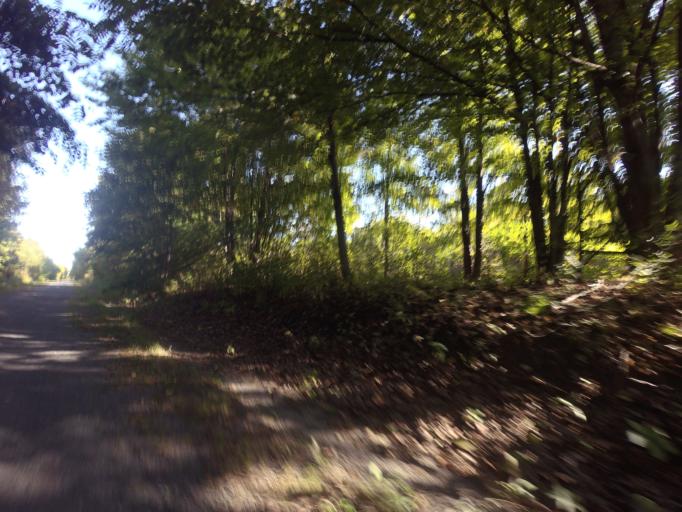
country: CA
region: Ontario
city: Hawkesbury
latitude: 45.5245
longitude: -74.5459
